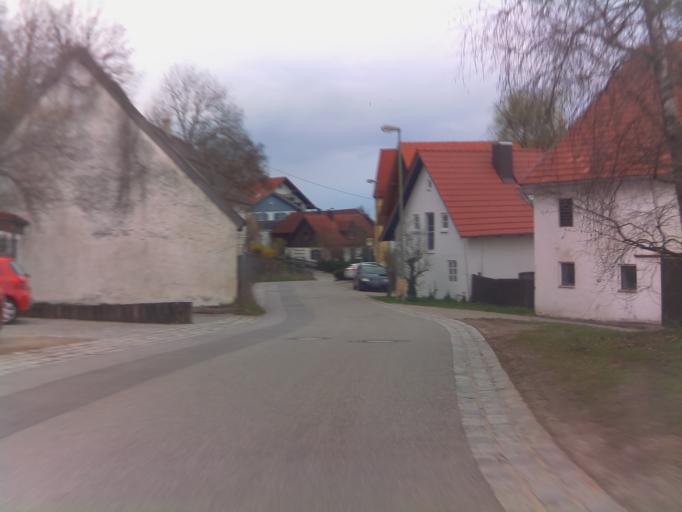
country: DE
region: Bavaria
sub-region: Upper Bavaria
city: Eresing
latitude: 48.0662
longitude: 10.9943
